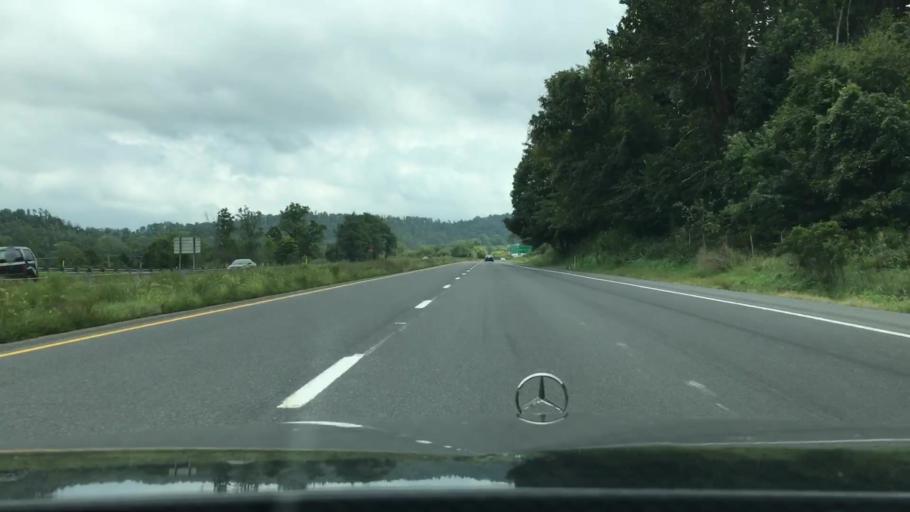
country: US
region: Maryland
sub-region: Washington County
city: Hancock
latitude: 39.7566
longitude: -78.1887
